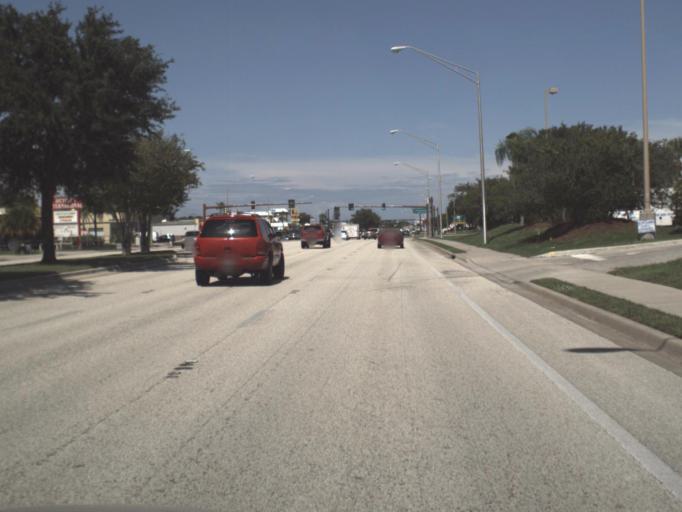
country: US
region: Florida
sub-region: Sarasota County
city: Venice Gardens
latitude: 27.0689
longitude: -82.4212
